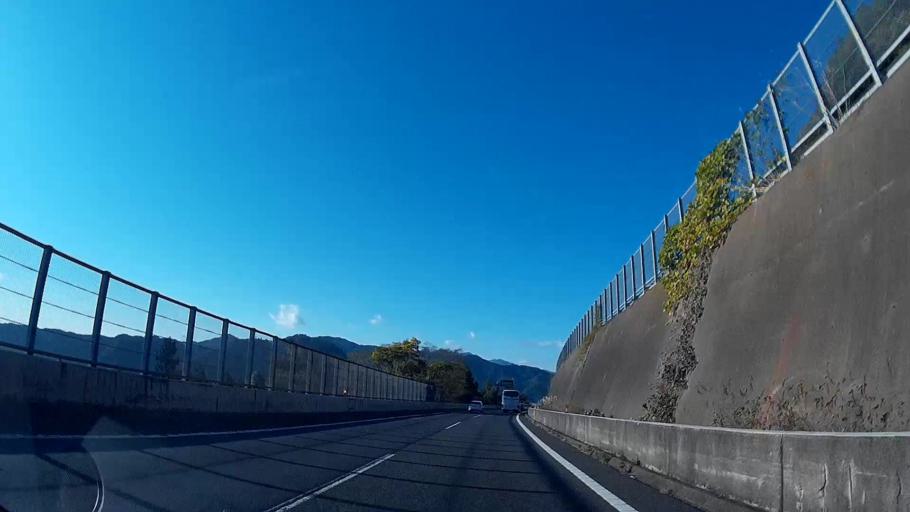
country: JP
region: Yamanashi
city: Uenohara
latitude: 35.6256
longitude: 139.2020
